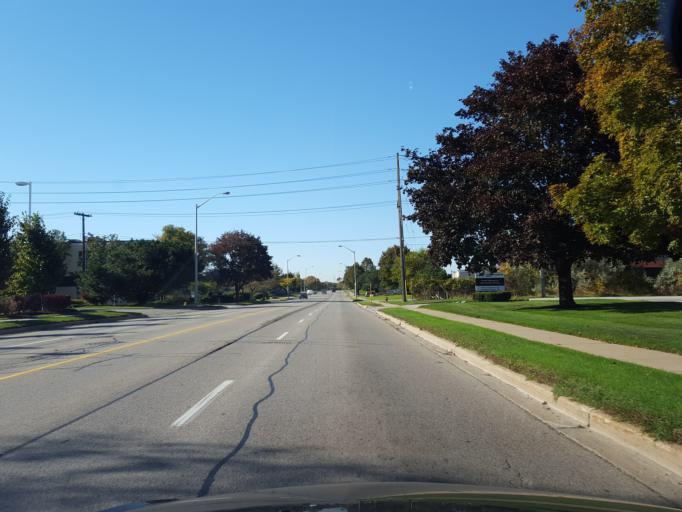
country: CA
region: Ontario
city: Burlington
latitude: 43.3635
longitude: -79.8041
